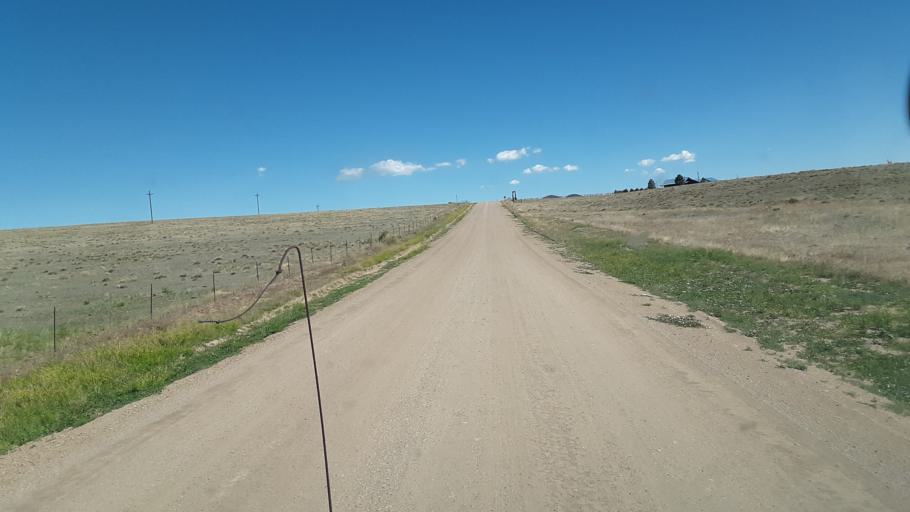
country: US
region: Colorado
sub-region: Custer County
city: Westcliffe
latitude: 38.2563
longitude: -105.4996
